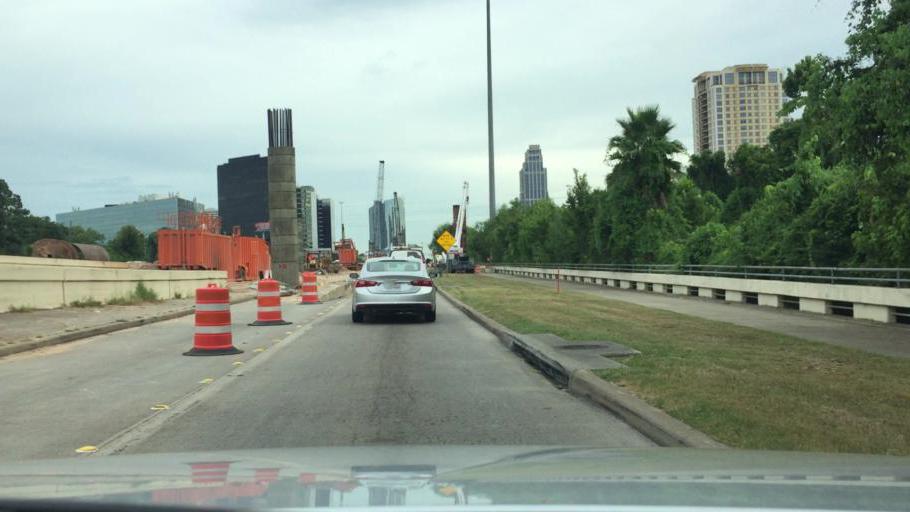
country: US
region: Texas
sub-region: Harris County
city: Hunters Creek Village
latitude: 29.7630
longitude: -95.4561
